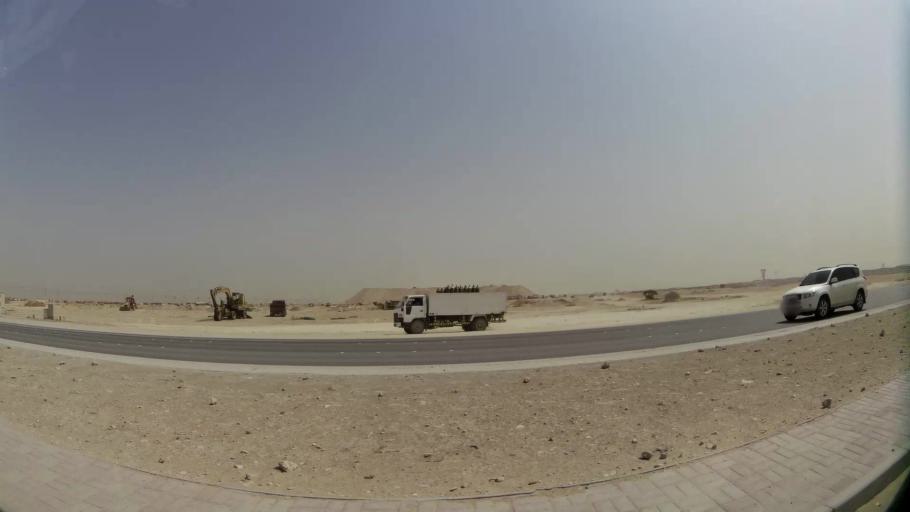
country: QA
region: Baladiyat ar Rayyan
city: Ar Rayyan
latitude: 25.1735
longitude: 51.3998
